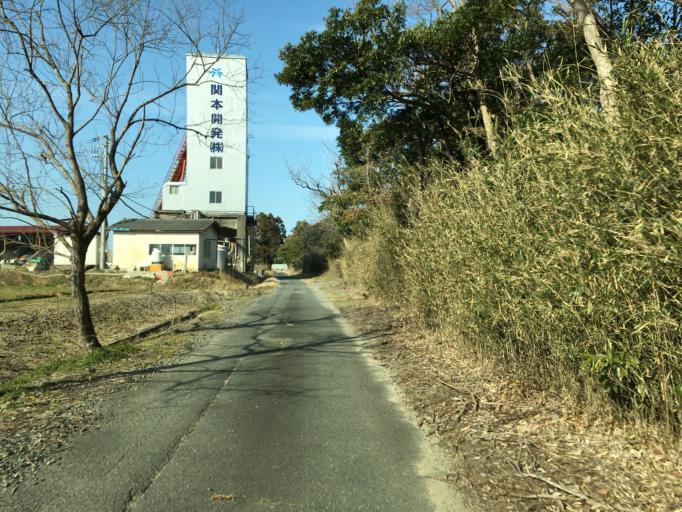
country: JP
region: Ibaraki
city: Takahagi
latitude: 36.7455
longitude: 140.7297
